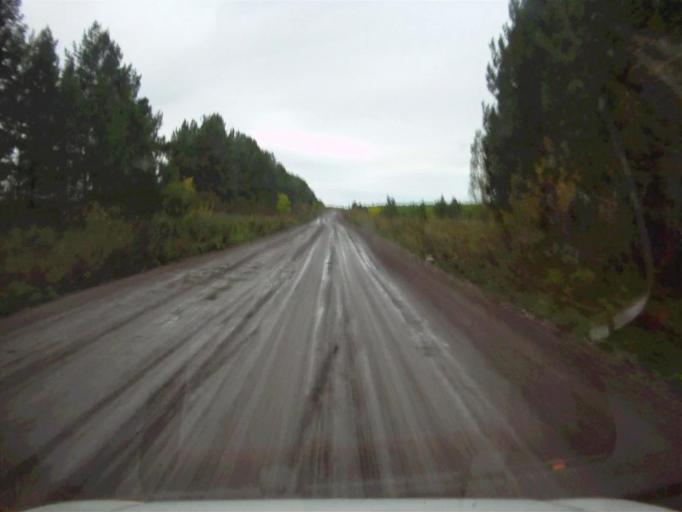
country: RU
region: Chelyabinsk
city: Nyazepetrovsk
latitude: 56.1436
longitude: 59.2866
